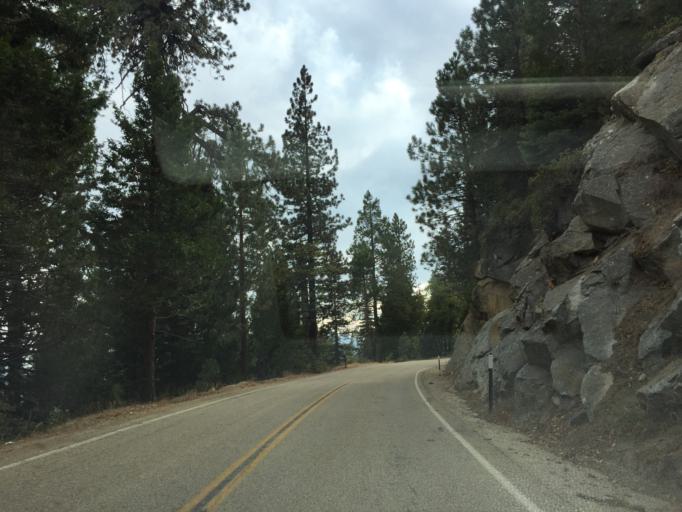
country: US
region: California
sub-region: Tulare County
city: Three Rivers
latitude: 36.7206
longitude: -118.9169
